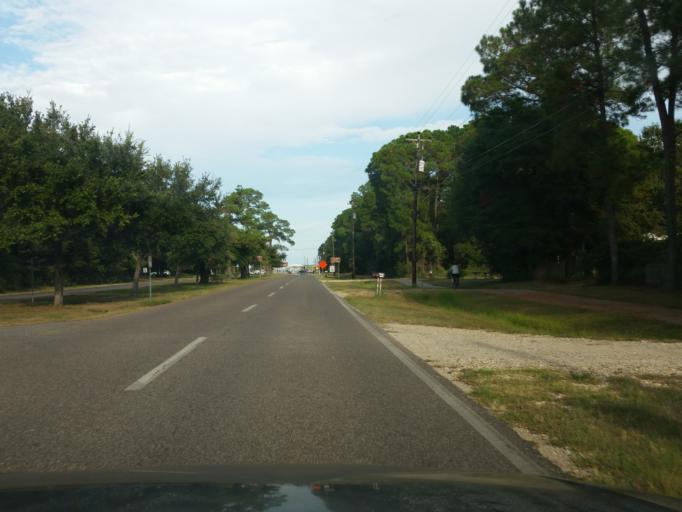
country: US
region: Alabama
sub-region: Mobile County
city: Dauphin Island
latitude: 30.2513
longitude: -88.0874
